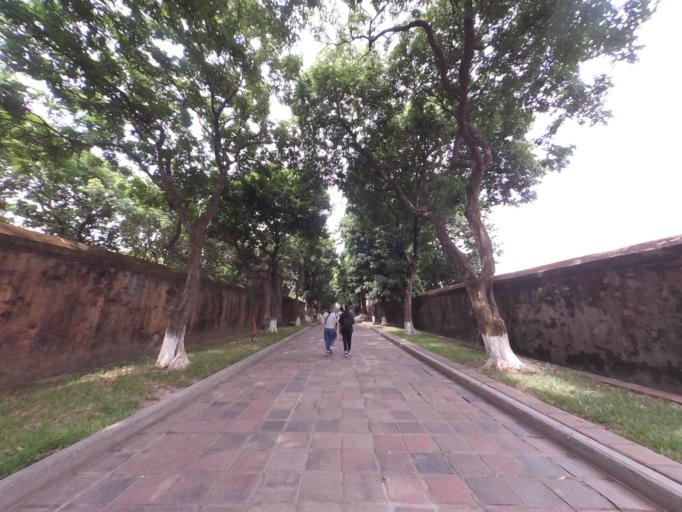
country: VN
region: Thua Thien-Hue
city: Hue
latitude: 16.4680
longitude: 107.5768
